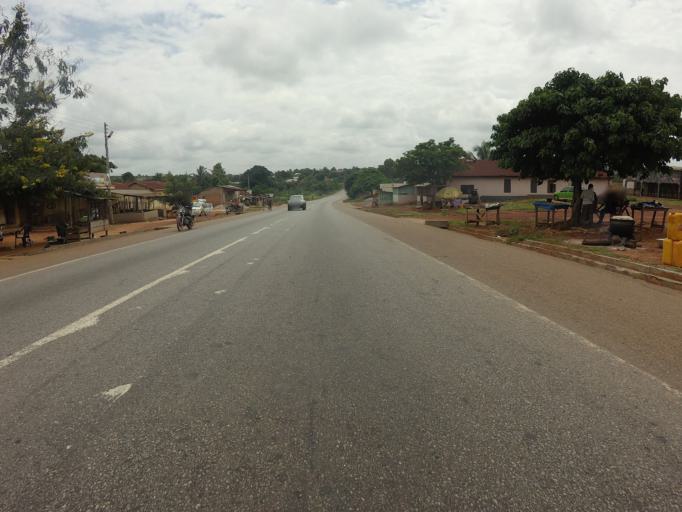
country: GH
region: Brong-Ahafo
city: Techiman
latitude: 7.4600
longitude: -1.9713
